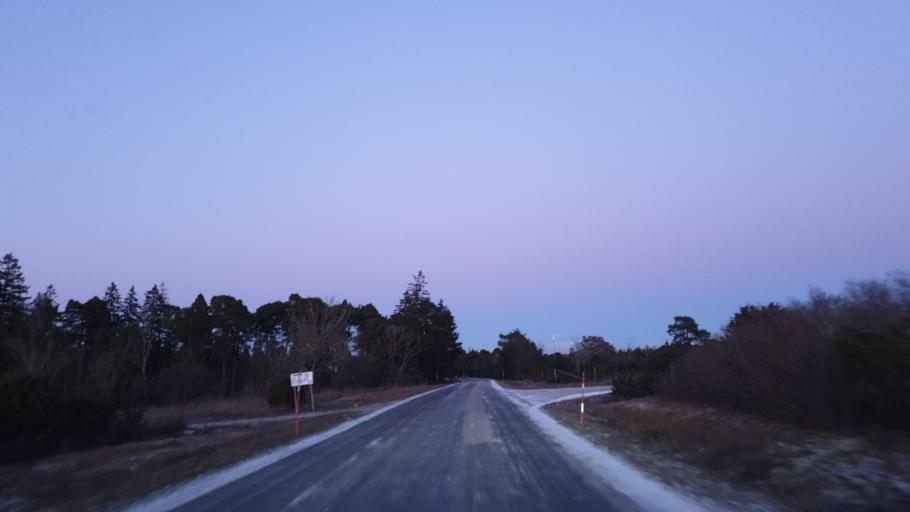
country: SE
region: Gotland
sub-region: Gotland
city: Slite
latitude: 57.4104
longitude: 18.8085
